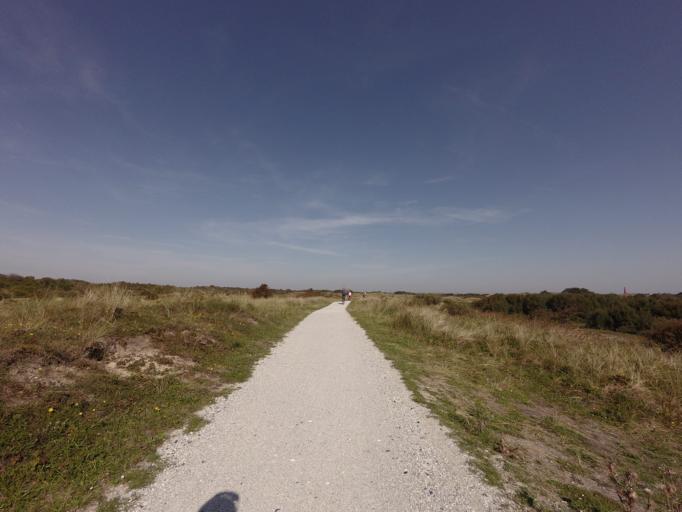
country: NL
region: Friesland
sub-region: Gemeente Schiermonnikoog
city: Schiermonnikoog
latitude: 53.4745
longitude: 6.1406
